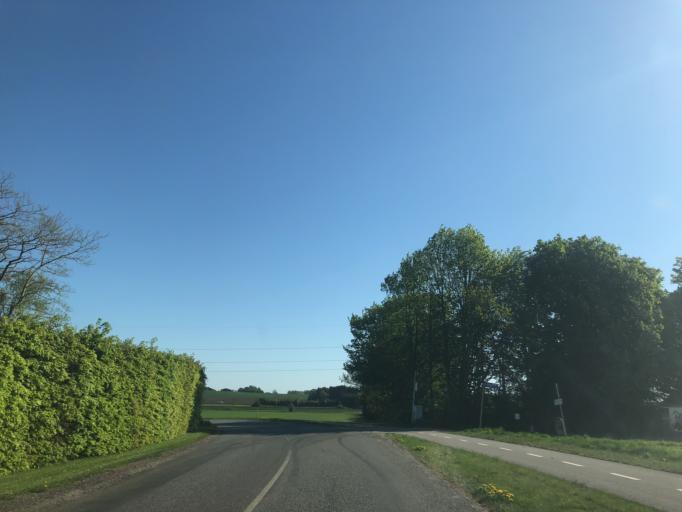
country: DK
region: Zealand
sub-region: Ringsted Kommune
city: Ringsted
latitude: 55.4411
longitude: 11.7270
